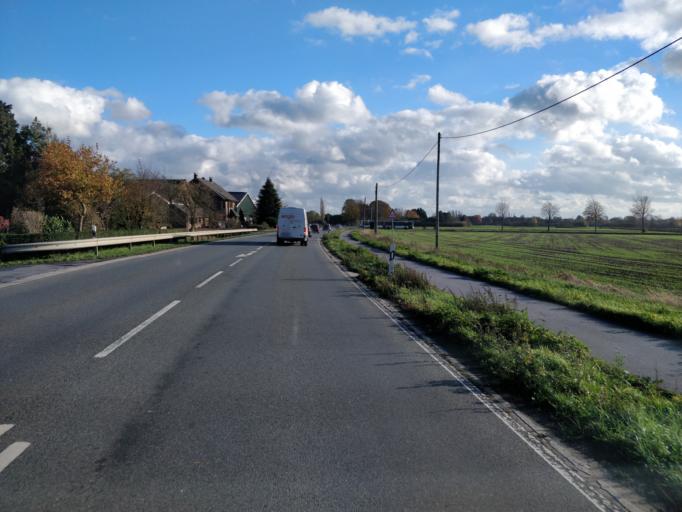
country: DE
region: North Rhine-Westphalia
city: Rees
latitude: 51.7742
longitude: 6.3832
